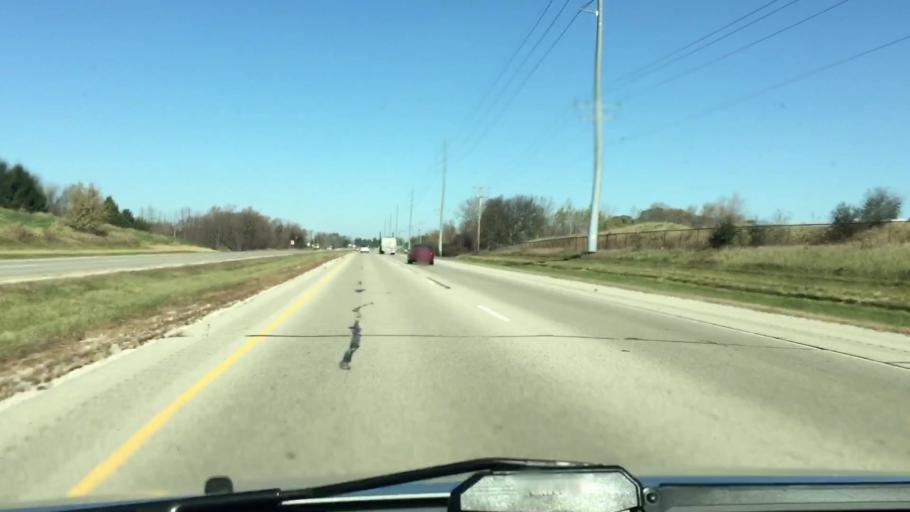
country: US
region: Wisconsin
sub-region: Waukesha County
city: Sussex
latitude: 43.0983
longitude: -88.2071
